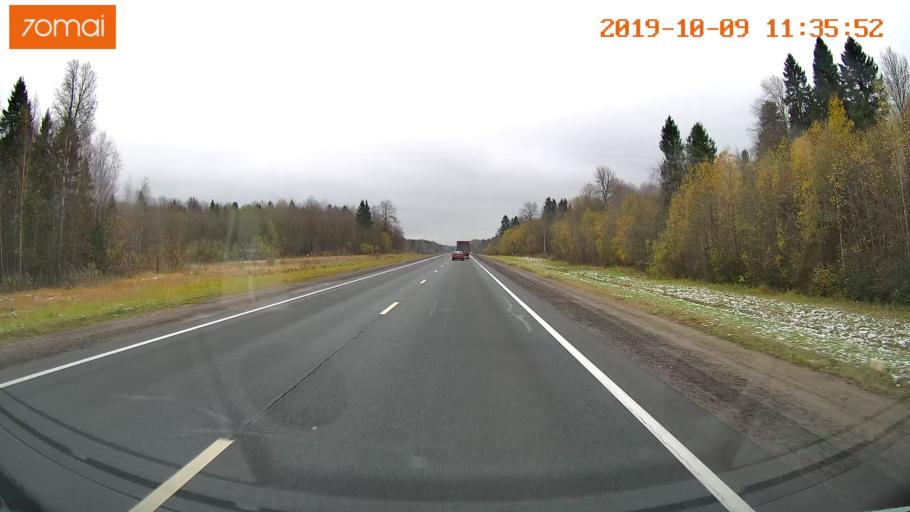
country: RU
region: Vologda
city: Gryazovets
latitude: 58.9981
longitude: 40.1305
